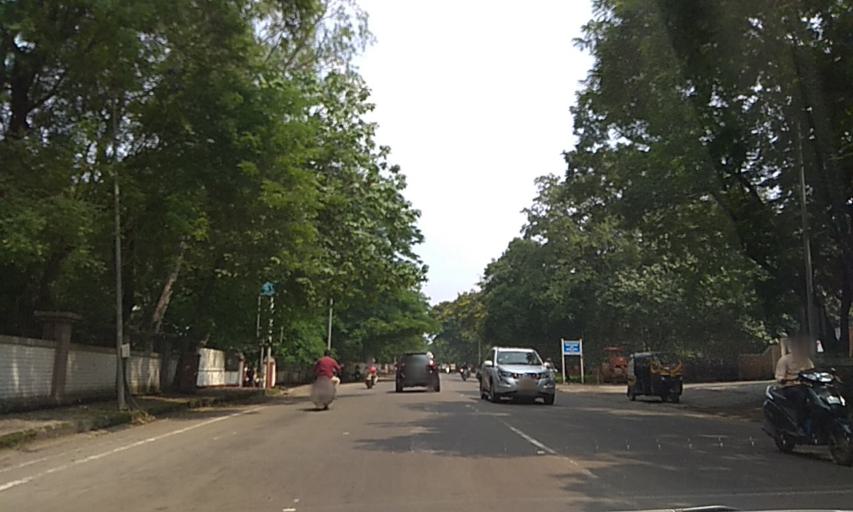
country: IN
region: Maharashtra
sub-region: Pune Division
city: Shivaji Nagar
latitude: 18.5410
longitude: 73.8216
